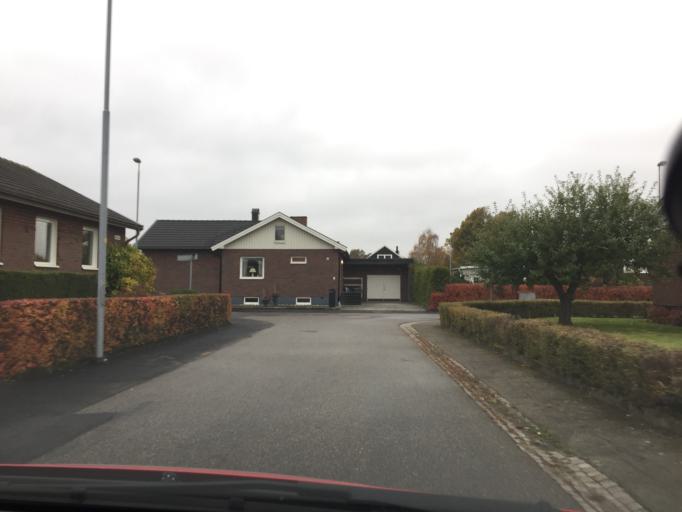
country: SE
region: Vaestra Goetaland
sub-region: Trollhattan
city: Trollhattan
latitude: 58.2797
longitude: 12.3215
